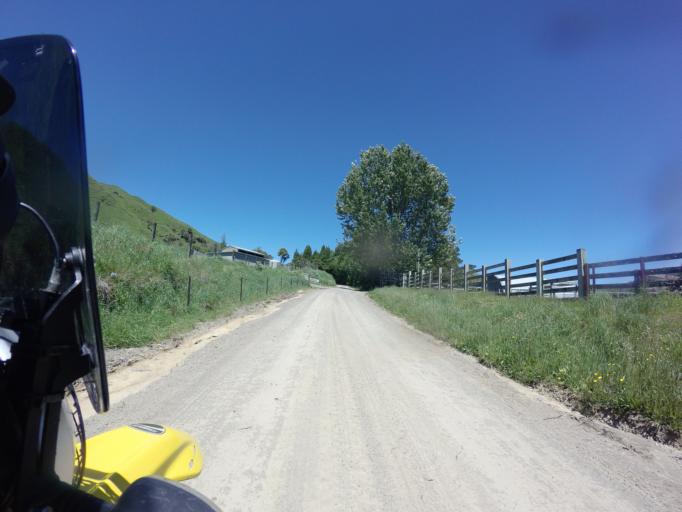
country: NZ
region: Bay of Plenty
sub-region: Opotiki District
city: Opotiki
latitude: -38.3973
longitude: 177.4588
